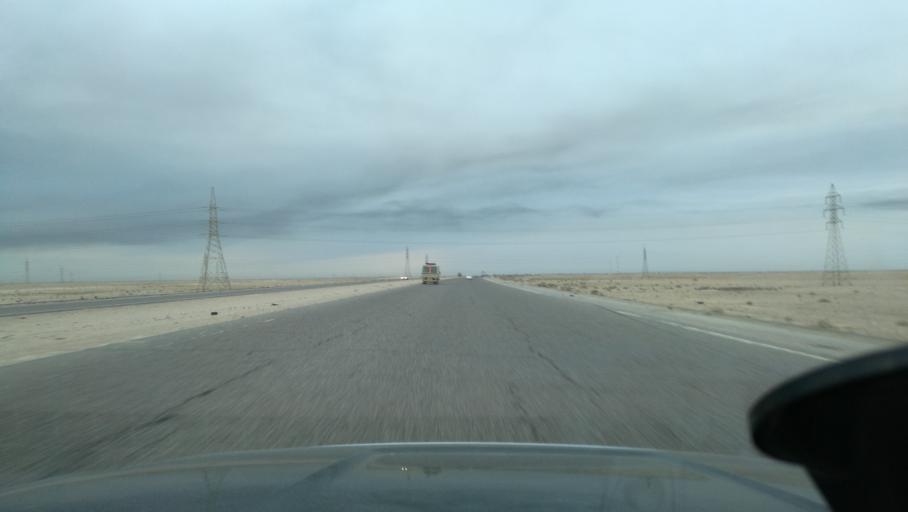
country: IQ
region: Basra Governorate
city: Az Zubayr
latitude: 30.4598
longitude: 47.3672
